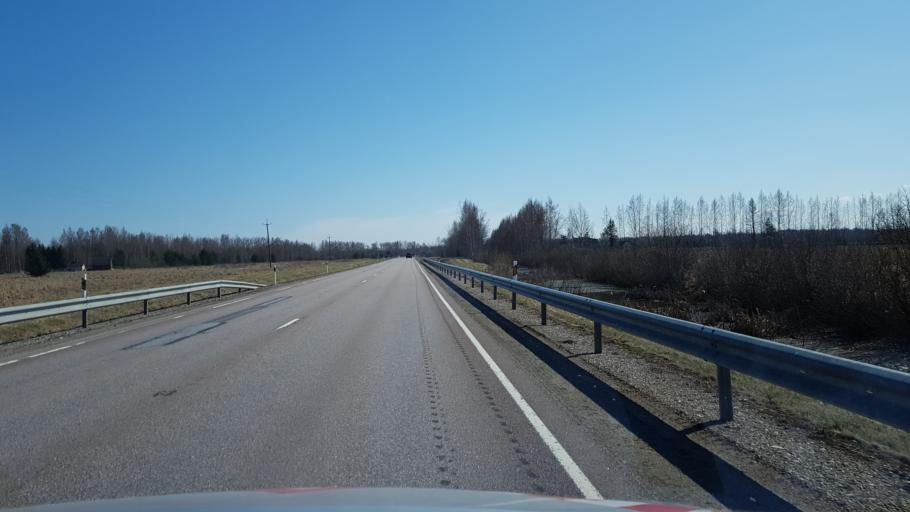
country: EE
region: Jogevamaa
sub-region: Mustvee linn
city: Mustvee
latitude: 58.8001
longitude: 26.9414
